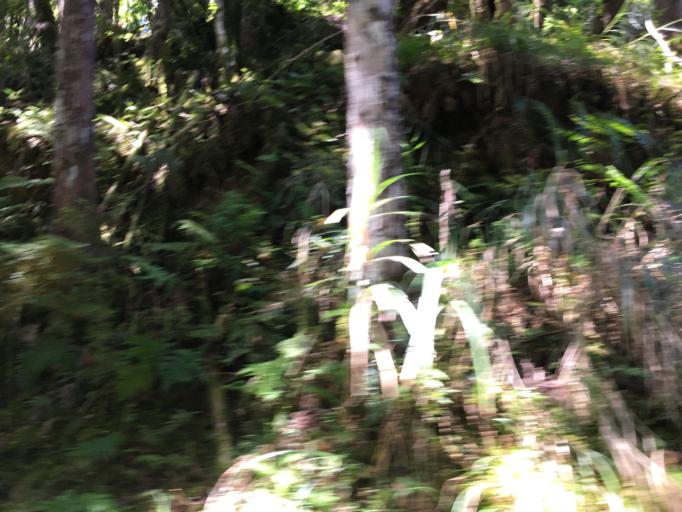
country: TW
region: Taiwan
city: Daxi
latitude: 24.5546
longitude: 121.3970
